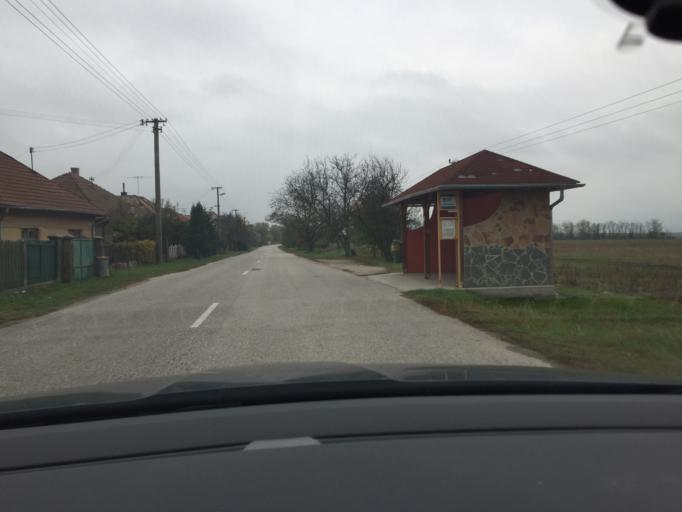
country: HU
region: Komarom-Esztergom
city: Esztergom
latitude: 47.9306
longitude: 18.7476
